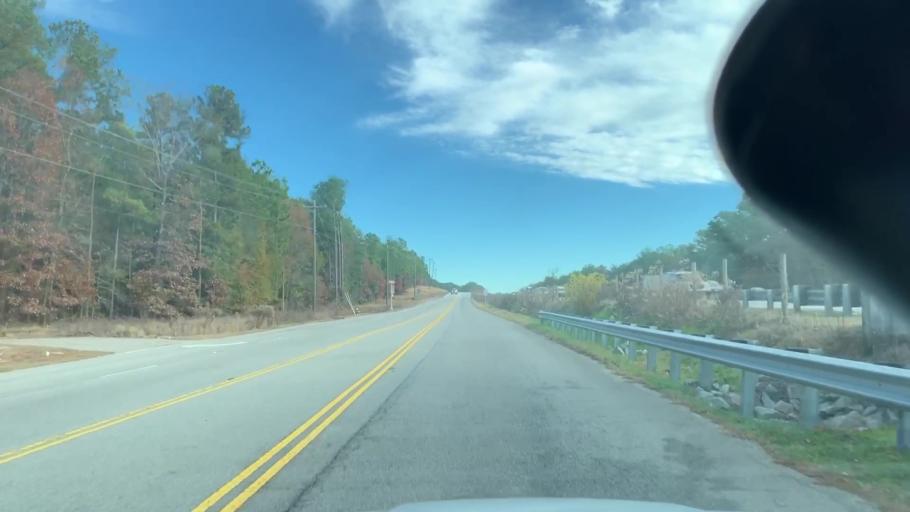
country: US
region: South Carolina
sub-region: Richland County
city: Woodfield
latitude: 34.0742
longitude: -80.9080
